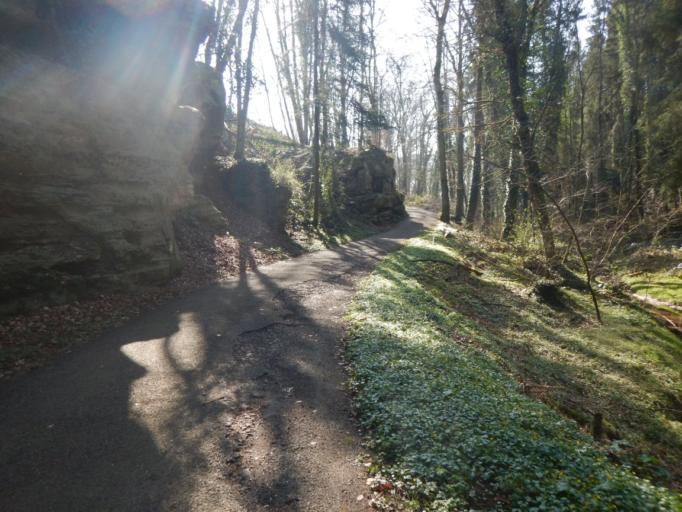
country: LU
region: Grevenmacher
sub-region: Canton d'Echternach
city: Consdorf
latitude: 49.7822
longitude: 6.3614
